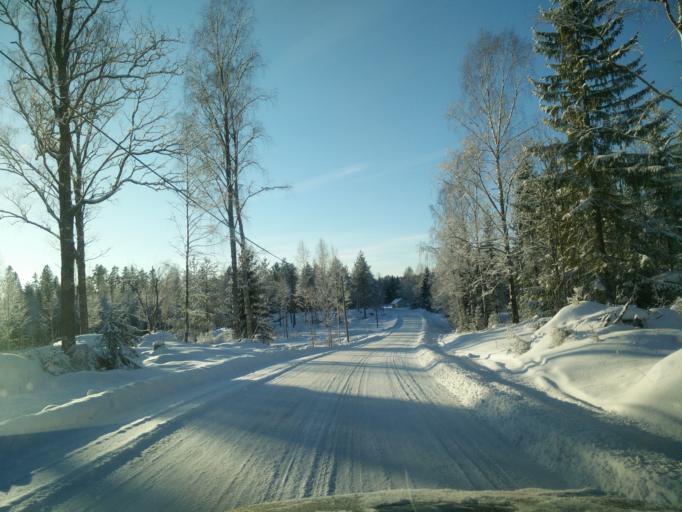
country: SE
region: Vaesternorrland
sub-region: Sundsvalls Kommun
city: Njurundabommen
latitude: 62.2333
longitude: 17.5107
